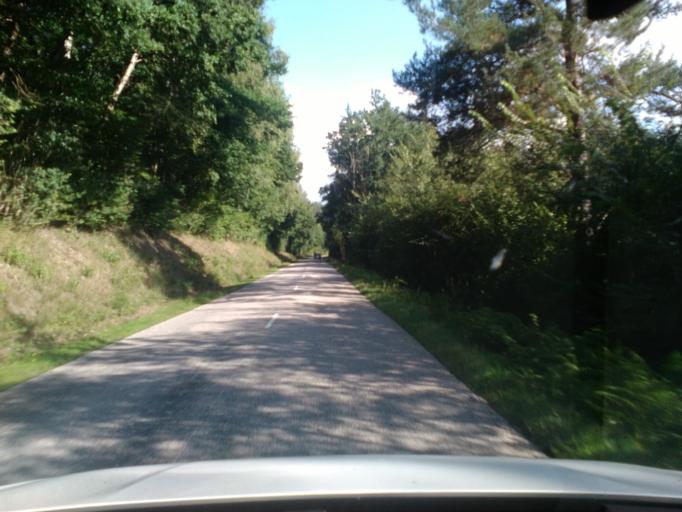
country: FR
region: Lorraine
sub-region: Departement des Vosges
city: Taintrux
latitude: 48.2363
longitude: 6.8991
